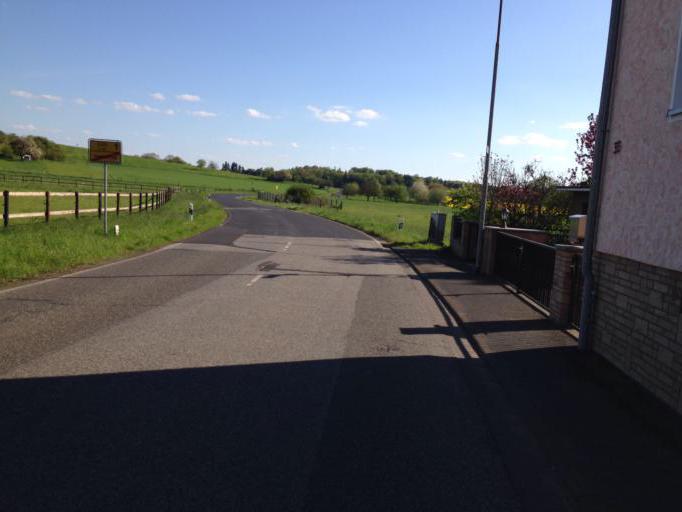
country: DE
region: Hesse
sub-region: Regierungsbezirk Giessen
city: Reiskirchen
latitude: 50.5734
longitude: 8.8484
